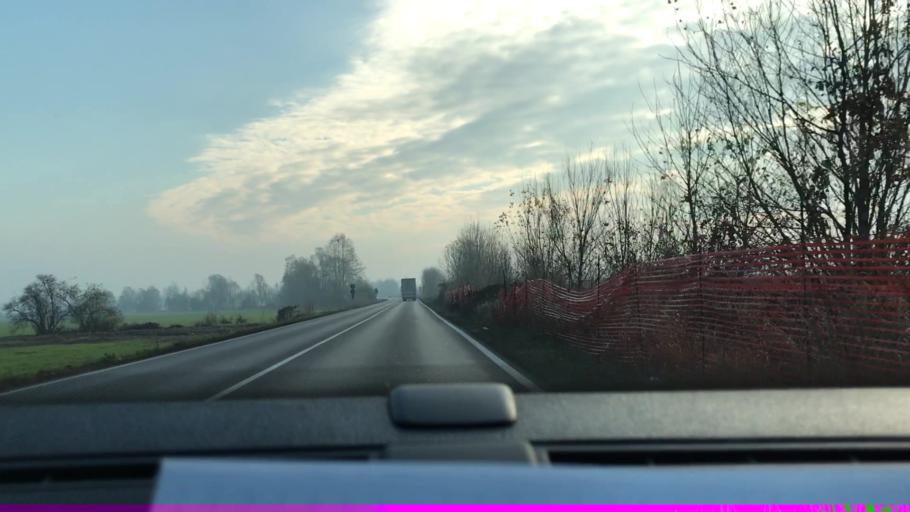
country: IT
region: Lombardy
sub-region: Provincia di Brescia
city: Pievedizio
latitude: 45.4896
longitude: 10.0968
